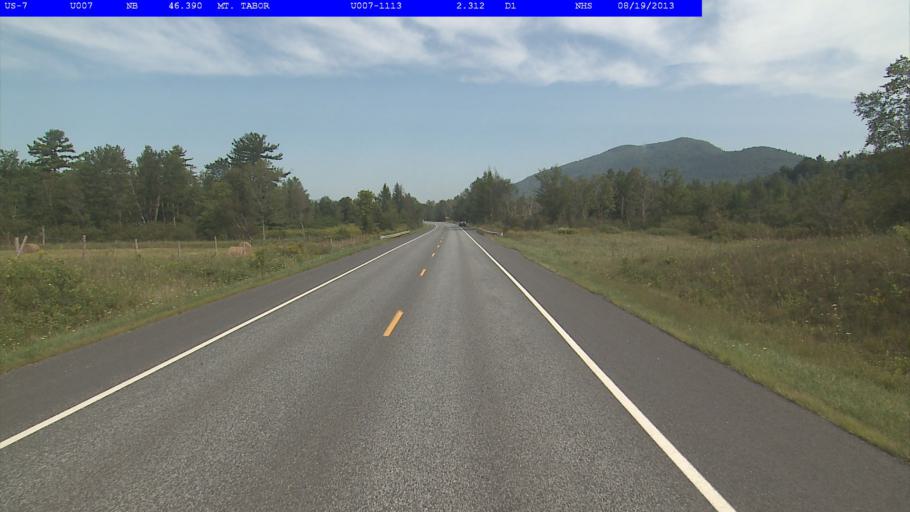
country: US
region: Vermont
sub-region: Bennington County
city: Manchester Center
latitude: 43.3383
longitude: -72.9921
